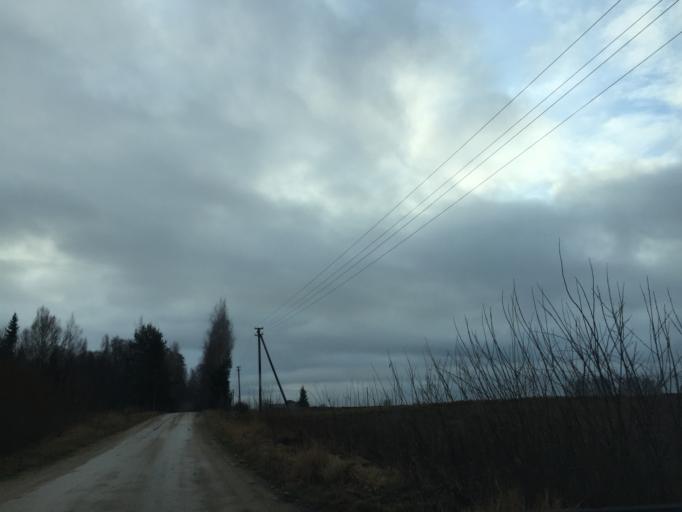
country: LV
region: Vainode
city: Vainode
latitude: 56.6078
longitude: 21.7987
